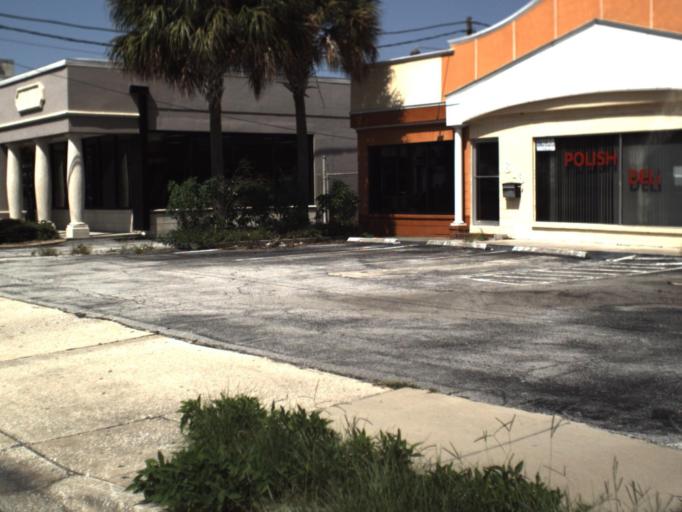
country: US
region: Florida
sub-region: Pinellas County
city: Clearwater
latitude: 27.9588
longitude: -82.7875
